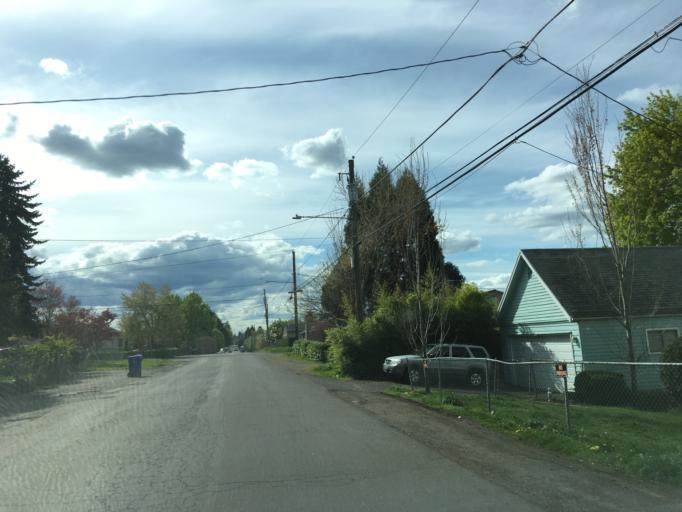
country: US
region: Oregon
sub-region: Multnomah County
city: Lents
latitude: 45.5572
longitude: -122.5497
